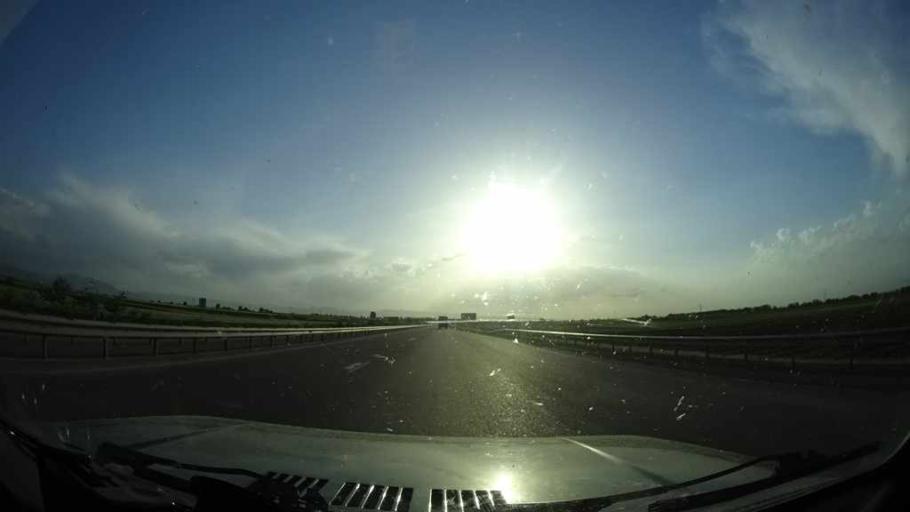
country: AZ
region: Samux
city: Samux
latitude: 40.6897
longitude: 46.5084
